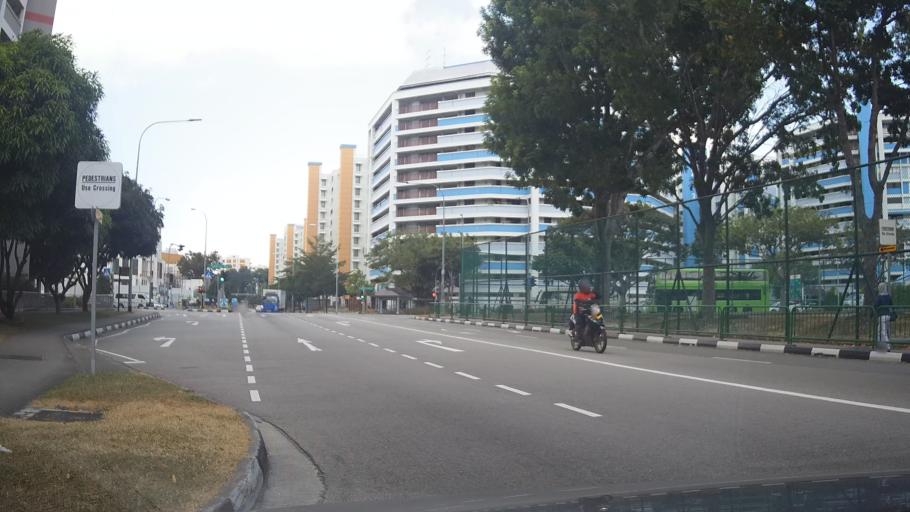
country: SG
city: Singapore
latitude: 1.3539
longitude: 103.9561
